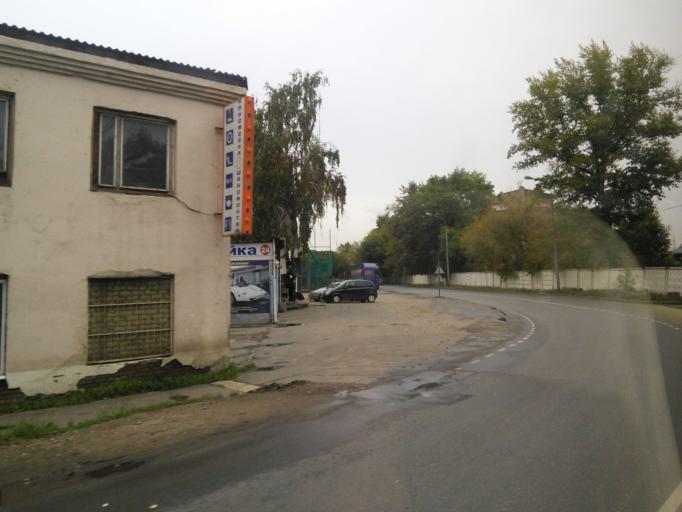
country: RU
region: Moskovskaya
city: Koptevo
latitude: 55.8380
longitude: 37.5145
